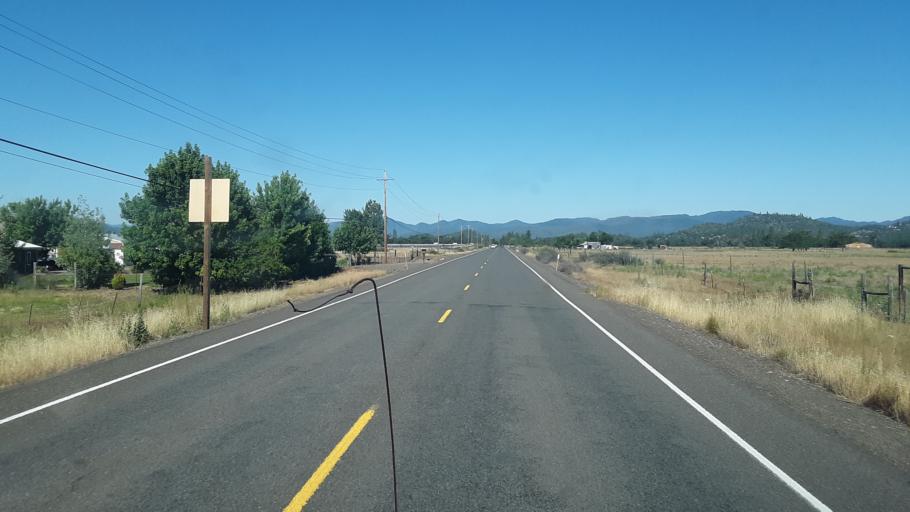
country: US
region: Oregon
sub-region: Jackson County
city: Eagle Point
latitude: 42.5237
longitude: -122.8196
